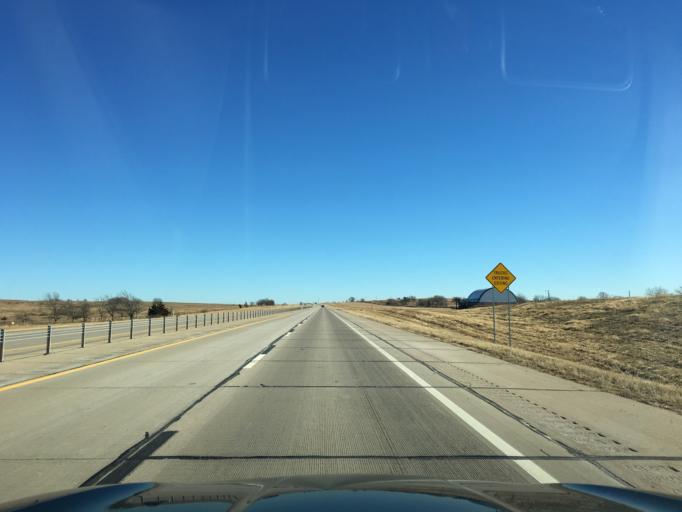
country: US
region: Oklahoma
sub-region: Noble County
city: Perry
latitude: 36.3926
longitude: -97.1914
